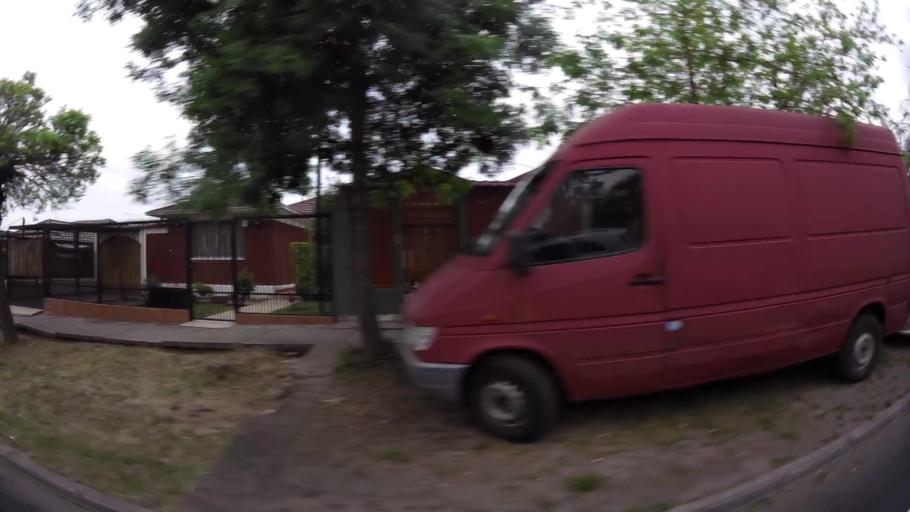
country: CL
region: Santiago Metropolitan
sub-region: Provincia de Santiago
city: Lo Prado
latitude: -33.5061
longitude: -70.7465
